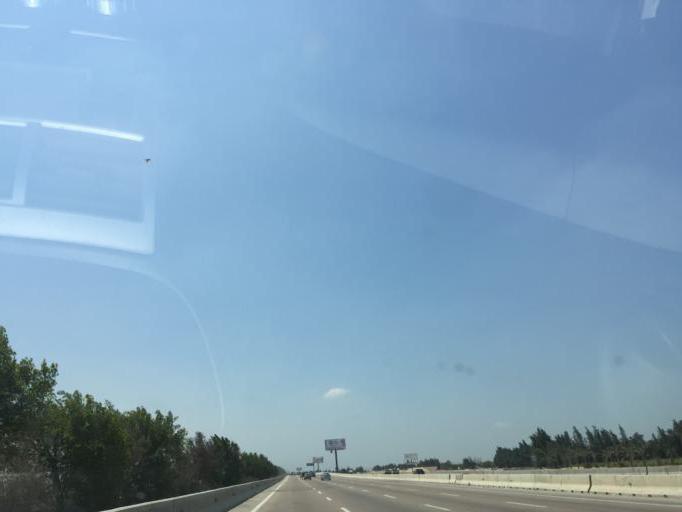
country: EG
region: Al Buhayrah
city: Beheira
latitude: 30.4341
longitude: 30.3355
